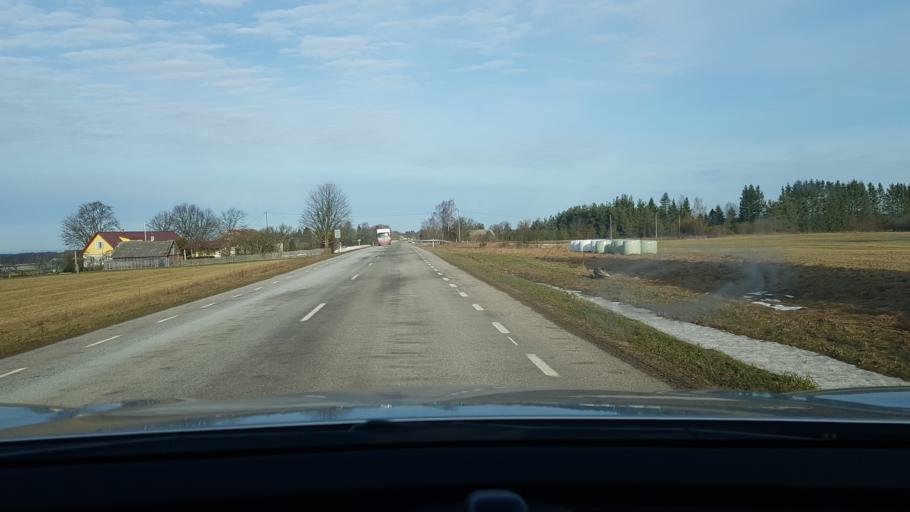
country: EE
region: Saare
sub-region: Kuressaare linn
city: Kuressaare
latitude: 58.5163
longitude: 22.7039
